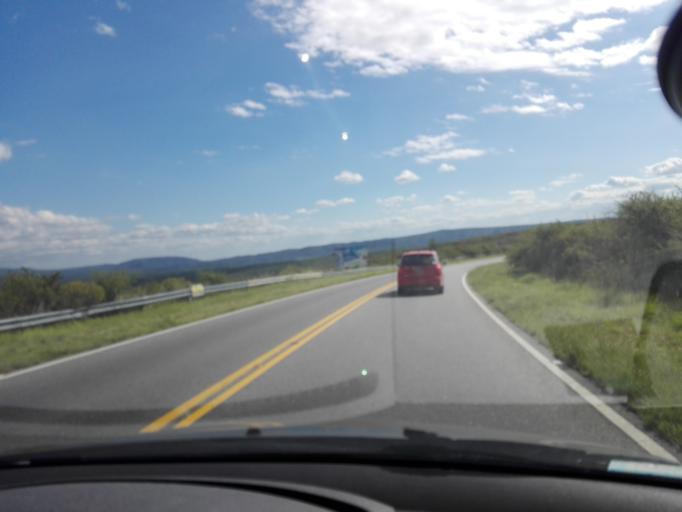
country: AR
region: Cordoba
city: Mina Clavero
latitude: -31.7629
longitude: -64.9644
